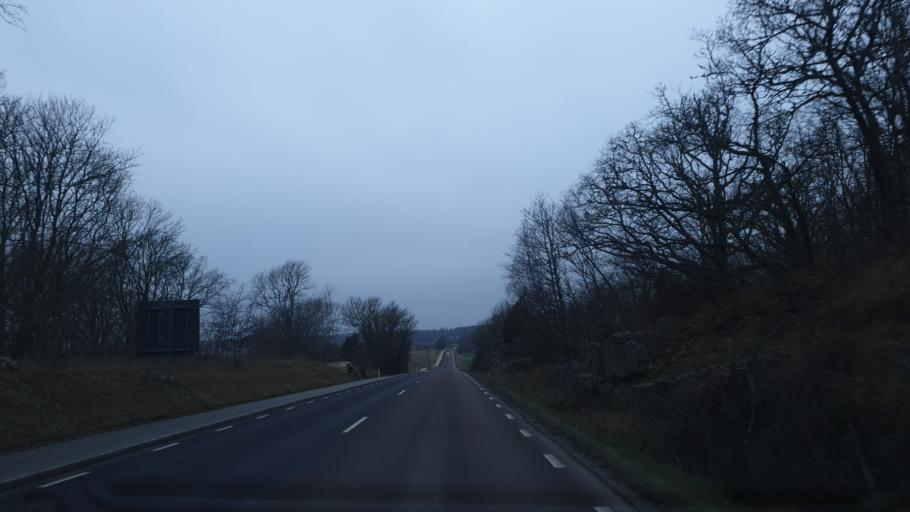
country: SE
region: Blekinge
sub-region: Karlskrona Kommun
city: Jaemjoe
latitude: 56.1712
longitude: 15.7361
